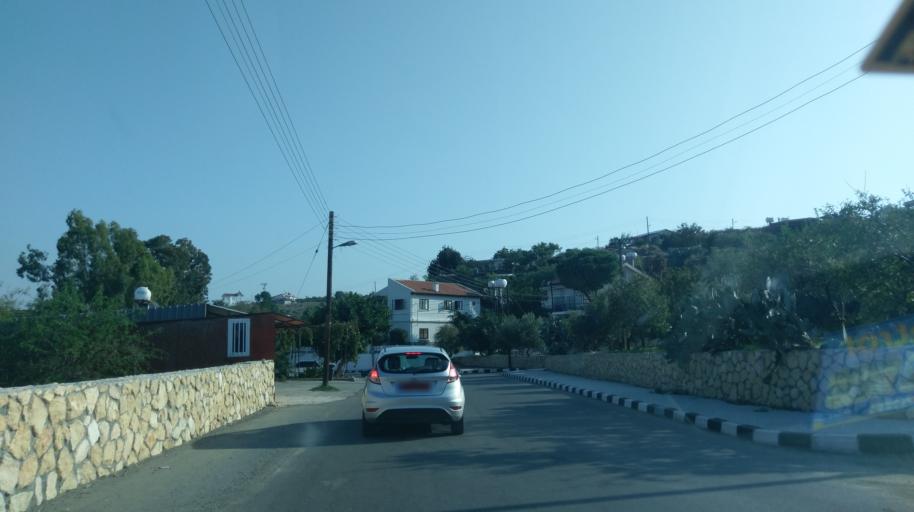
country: CY
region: Lefkosia
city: Lefka
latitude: 35.1504
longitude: 32.7980
